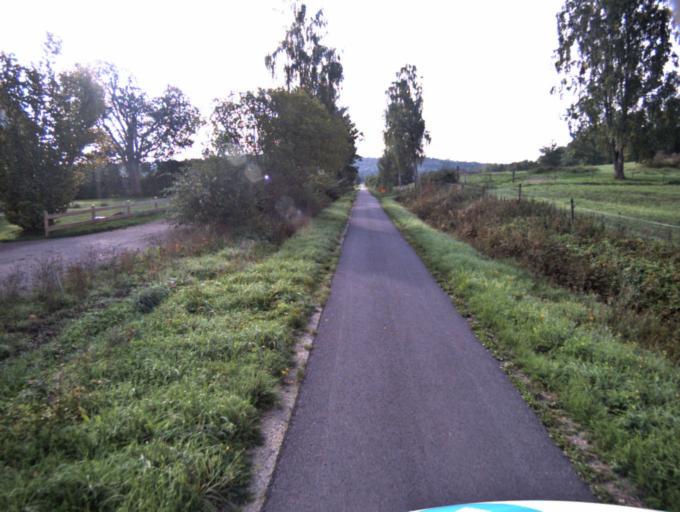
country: SE
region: Vaestra Goetaland
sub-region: Ulricehamns Kommun
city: Ulricehamn
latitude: 57.7393
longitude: 13.4020
